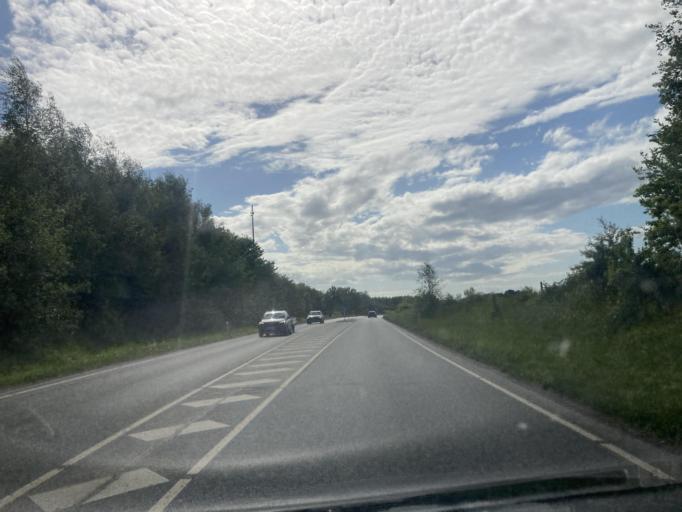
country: DK
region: Capital Region
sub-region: Gribskov Kommune
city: Helsinge
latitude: 56.0165
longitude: 12.1490
